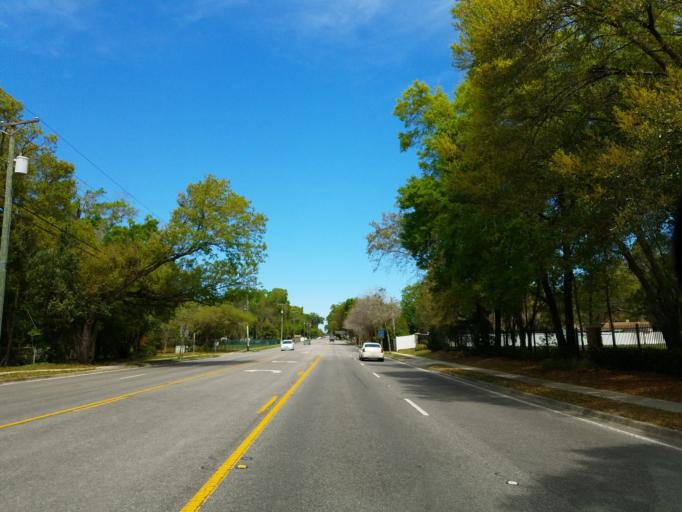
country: US
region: Florida
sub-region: Hillsborough County
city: Seffner
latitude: 27.9662
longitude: -82.2858
